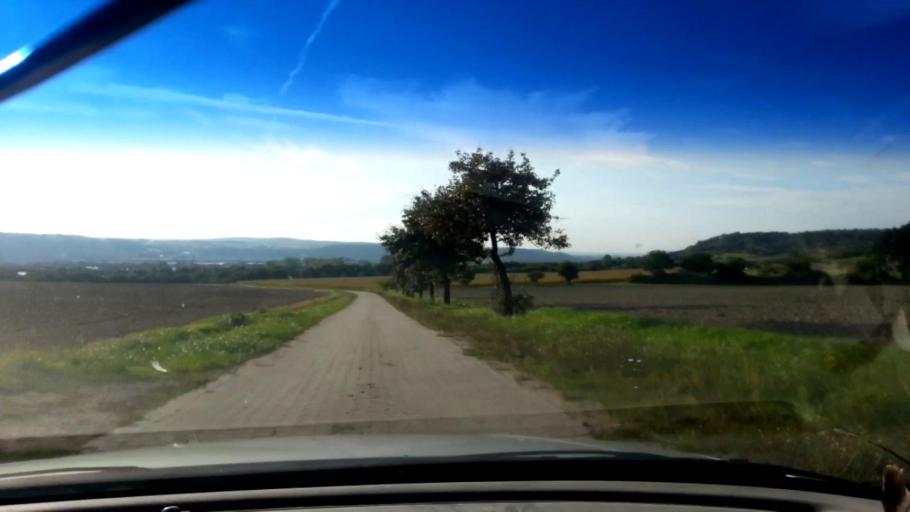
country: DE
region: Bavaria
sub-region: Upper Franconia
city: Lauter
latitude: 49.9479
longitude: 10.7647
